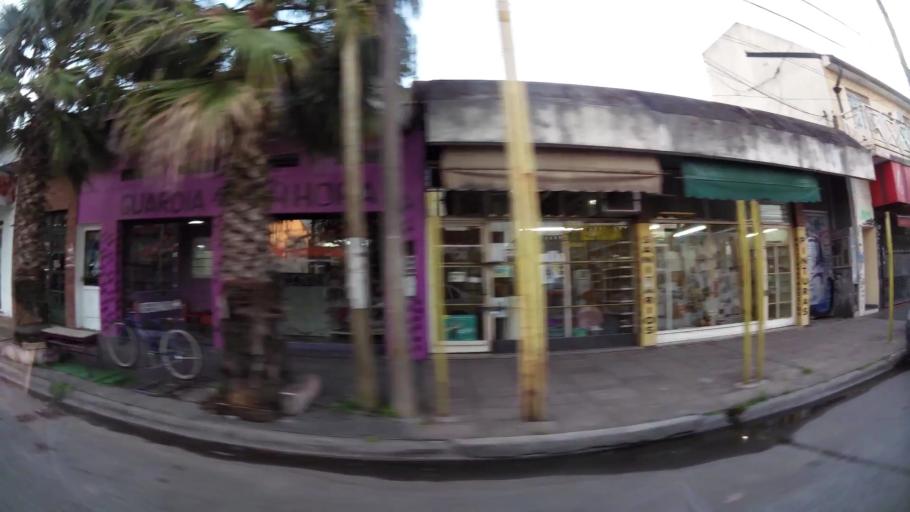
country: AR
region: Buenos Aires
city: Ituzaingo
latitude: -34.6501
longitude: -58.6485
